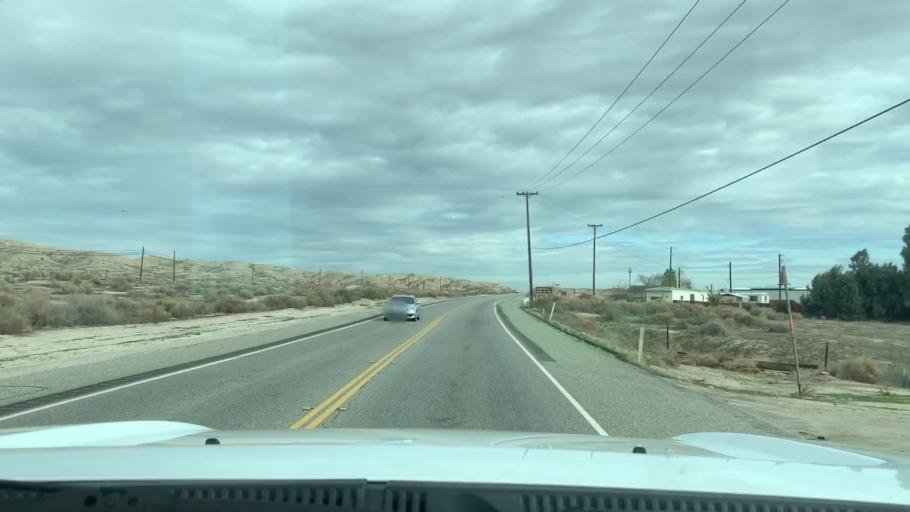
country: US
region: California
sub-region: Kern County
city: Ford City
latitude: 35.2314
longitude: -119.3726
